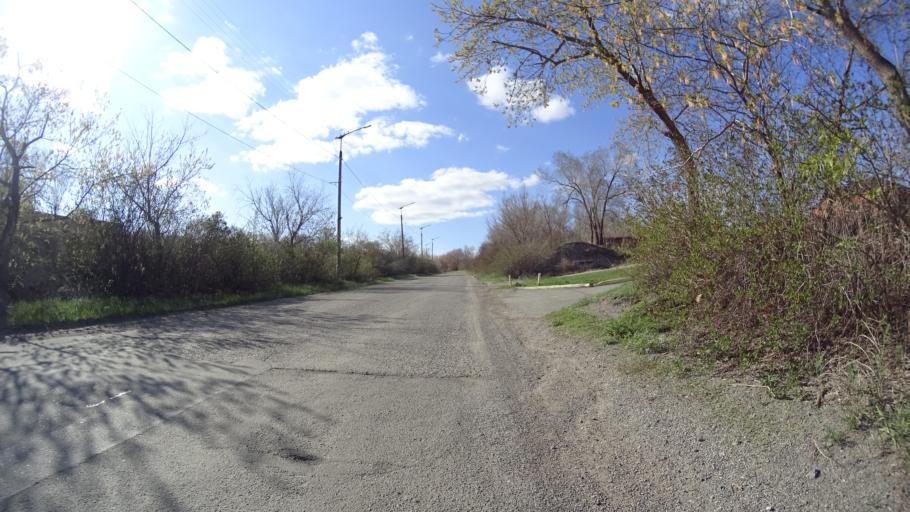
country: RU
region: Chelyabinsk
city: Troitsk
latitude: 54.0995
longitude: 61.5577
